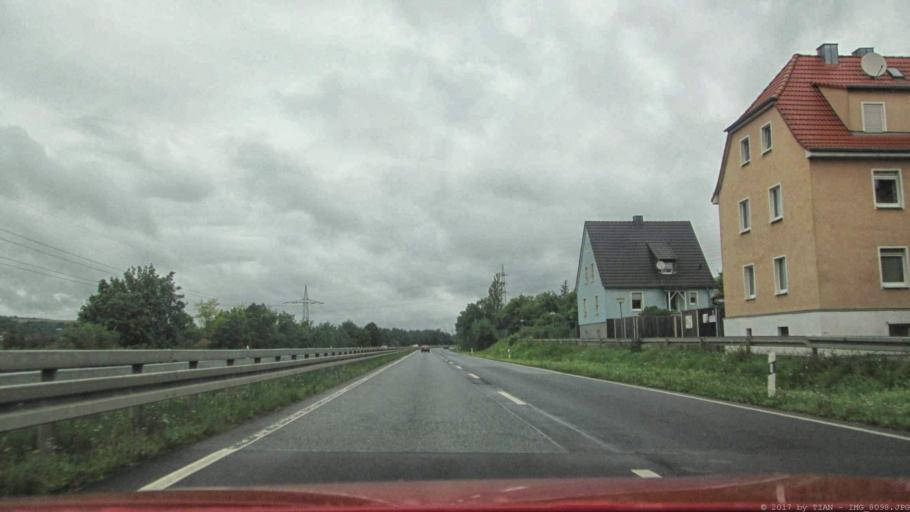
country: DE
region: Bavaria
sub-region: Regierungsbezirk Unterfranken
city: Zell am Main
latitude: 49.8172
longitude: 9.8790
